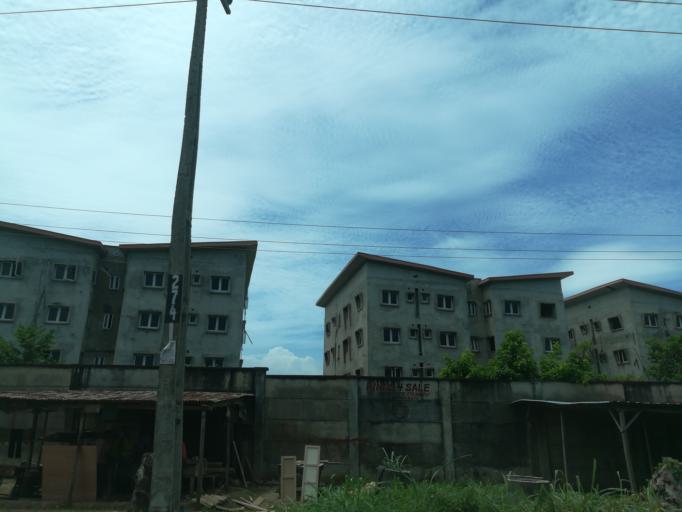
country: NG
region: Lagos
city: Ebute Ikorodu
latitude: 6.5715
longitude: 3.4836
